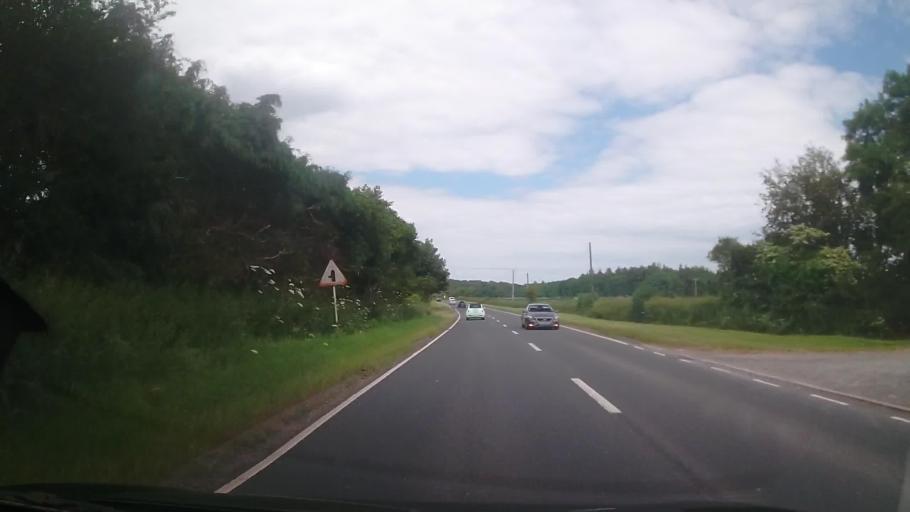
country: GB
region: England
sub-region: Herefordshire
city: Belmont
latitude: 52.0316
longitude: -2.7675
